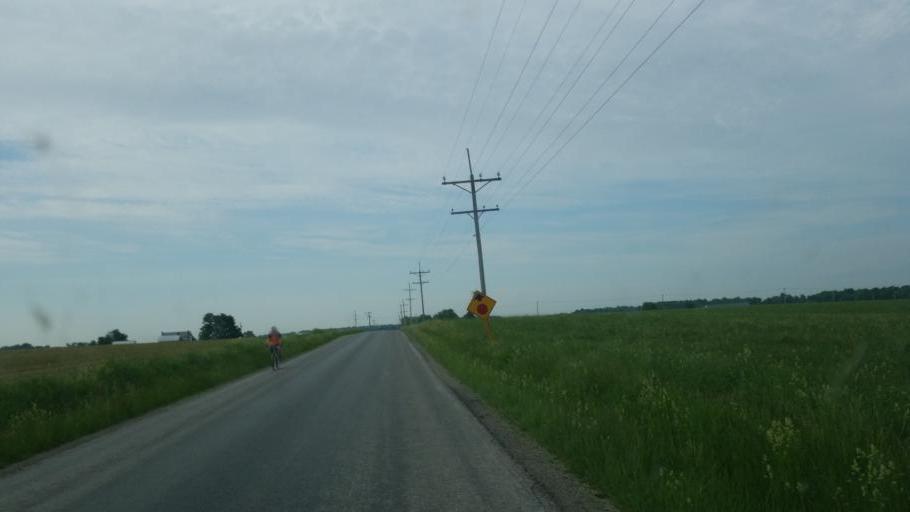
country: US
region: Ohio
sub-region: Wayne County
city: Dalton
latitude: 40.7585
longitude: -81.7549
